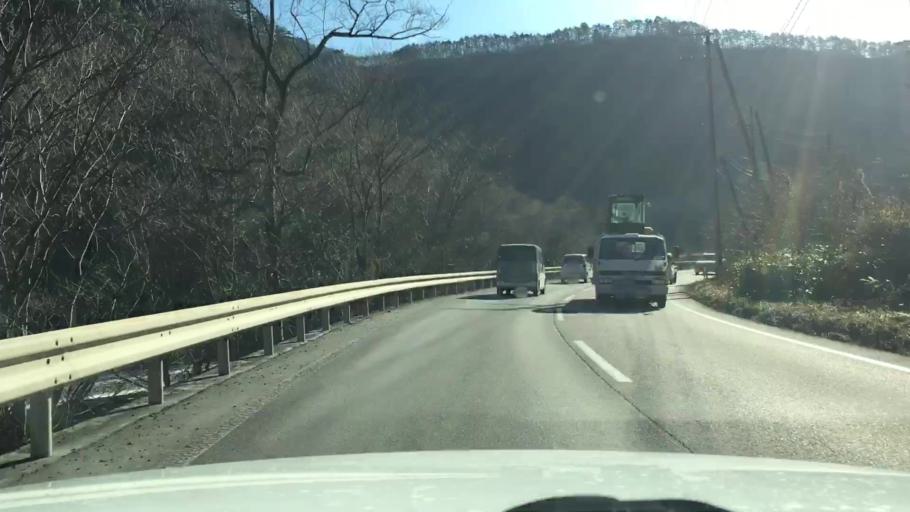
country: JP
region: Iwate
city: Miyako
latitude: 39.6101
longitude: 141.7882
